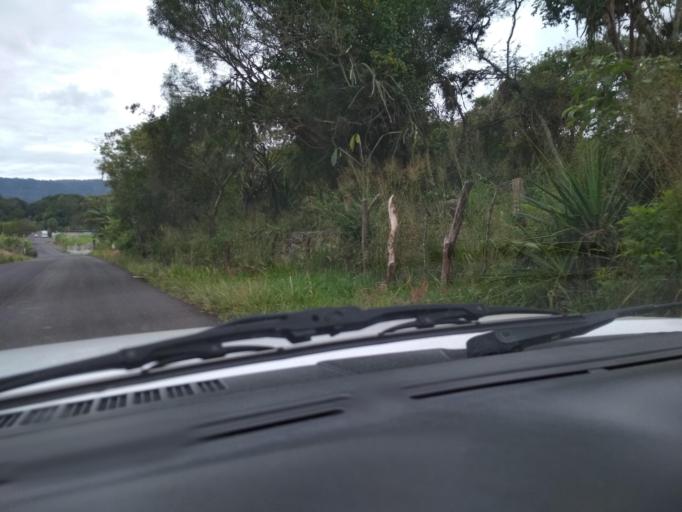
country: MX
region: Veracruz
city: Alto Lucero
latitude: 19.5910
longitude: -96.7877
